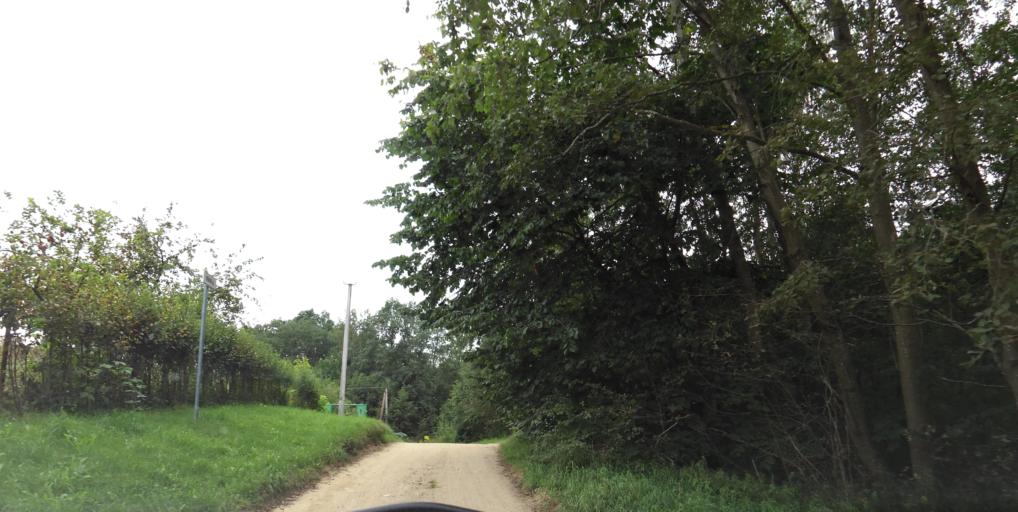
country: LT
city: Grigiskes
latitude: 54.7614
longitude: 25.0213
